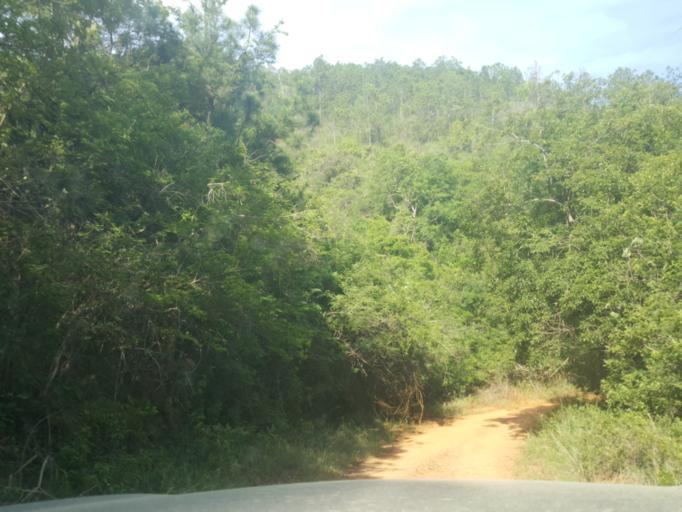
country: ZA
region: Limpopo
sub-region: Mopani District Municipality
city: Hoedspruit
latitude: -24.5914
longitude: 30.8362
